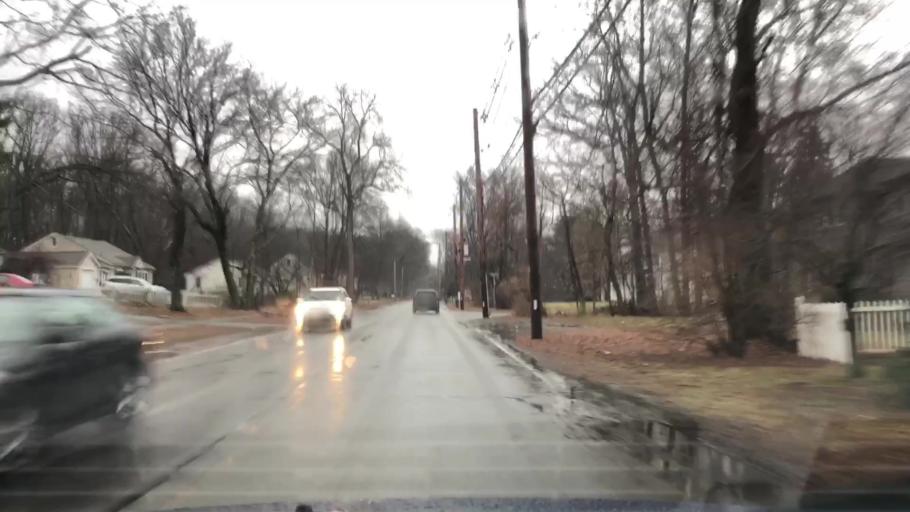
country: US
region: Massachusetts
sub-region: Essex County
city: North Andover
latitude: 42.6912
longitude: -71.1352
